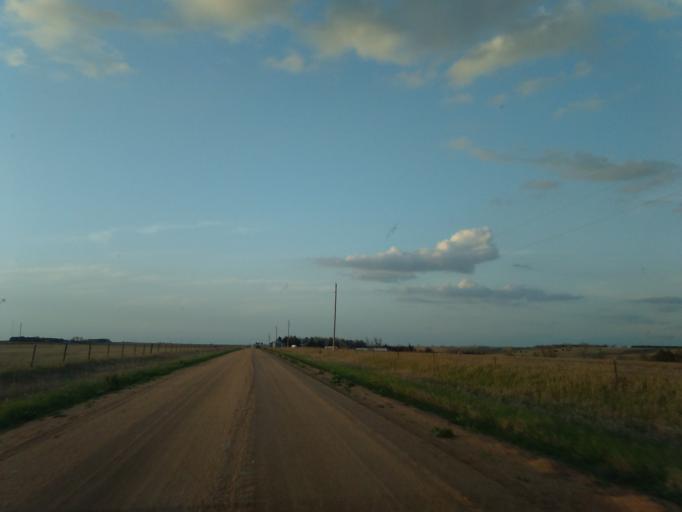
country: US
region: Nebraska
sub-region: Nuckolls County
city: Nelson
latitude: 40.2027
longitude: -98.2926
